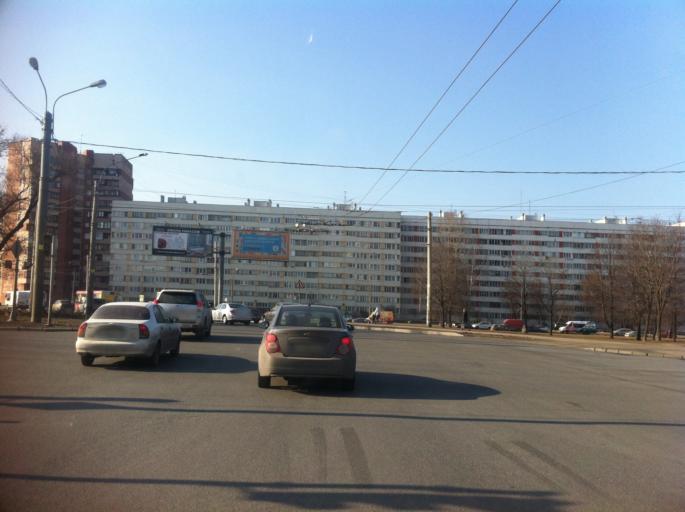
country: RU
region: St.-Petersburg
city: Dachnoye
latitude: 59.8522
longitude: 30.2384
